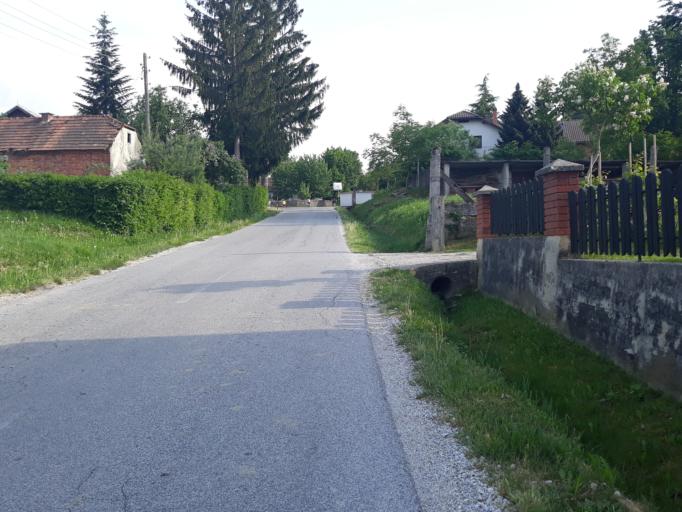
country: HR
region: Varazdinska
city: Ivanec
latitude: 46.2262
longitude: 16.1477
